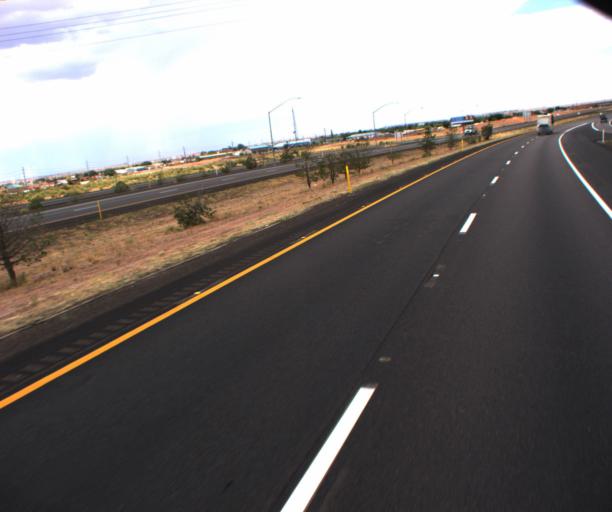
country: US
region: Arizona
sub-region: Navajo County
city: Winslow
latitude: 35.0191
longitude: -110.6764
